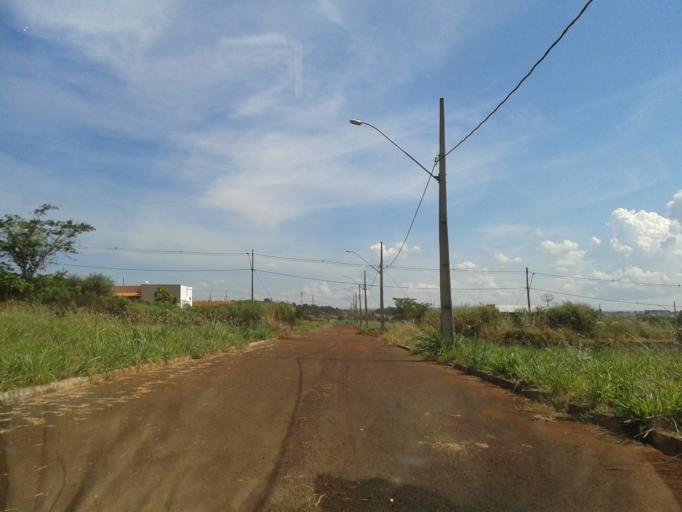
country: BR
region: Goias
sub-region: Itumbiara
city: Itumbiara
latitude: -18.4238
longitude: -49.1817
